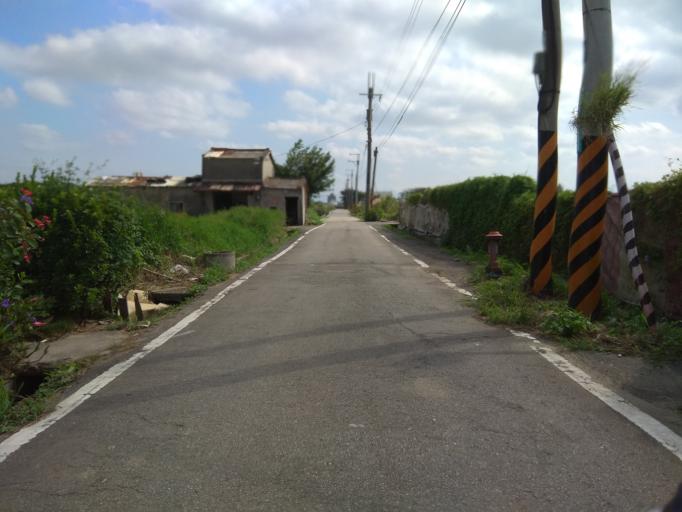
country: TW
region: Taiwan
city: Taoyuan City
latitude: 25.0625
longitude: 121.2169
